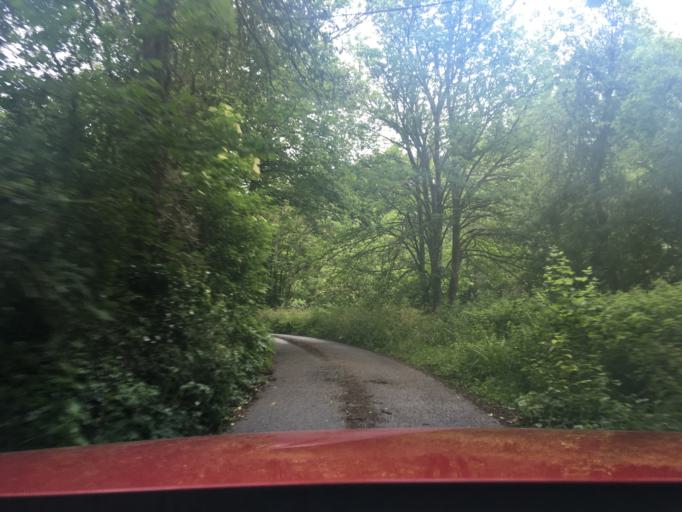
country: GB
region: England
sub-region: Gloucestershire
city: Shurdington
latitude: 51.7921
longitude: -2.0803
